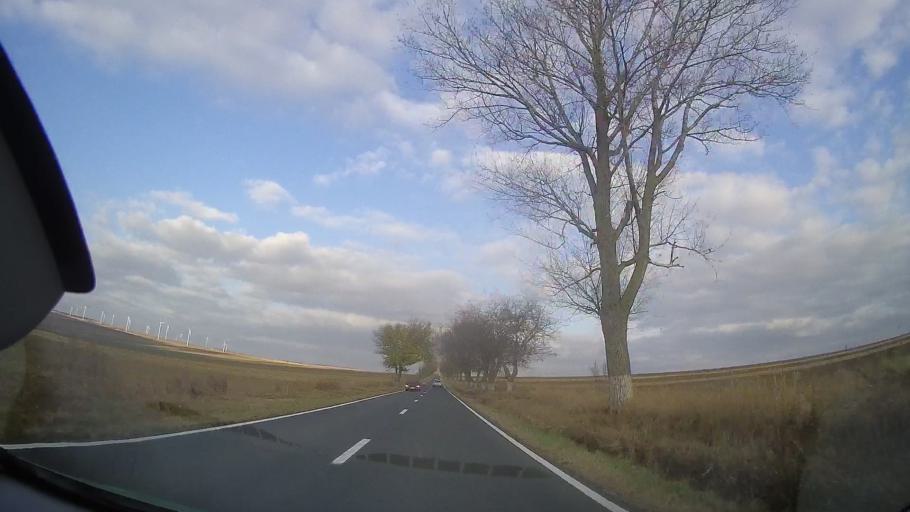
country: RO
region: Tulcea
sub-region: Comuna Topolog
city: Topolog
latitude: 44.8588
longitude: 28.3414
